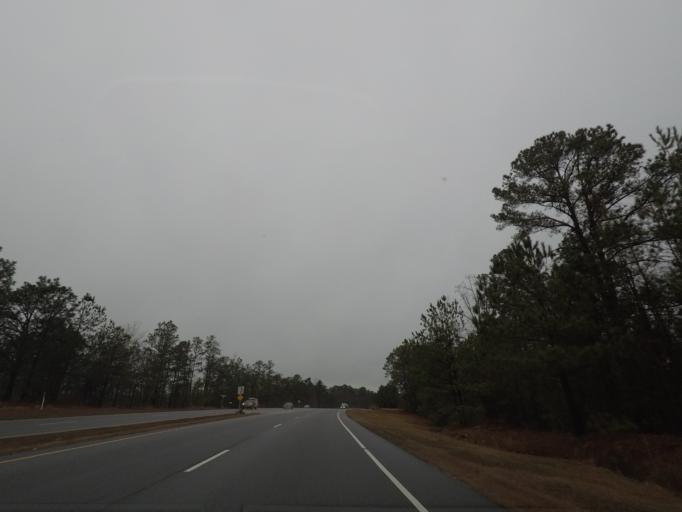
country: US
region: North Carolina
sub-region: Lee County
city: Broadway
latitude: 35.3430
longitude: -79.1045
